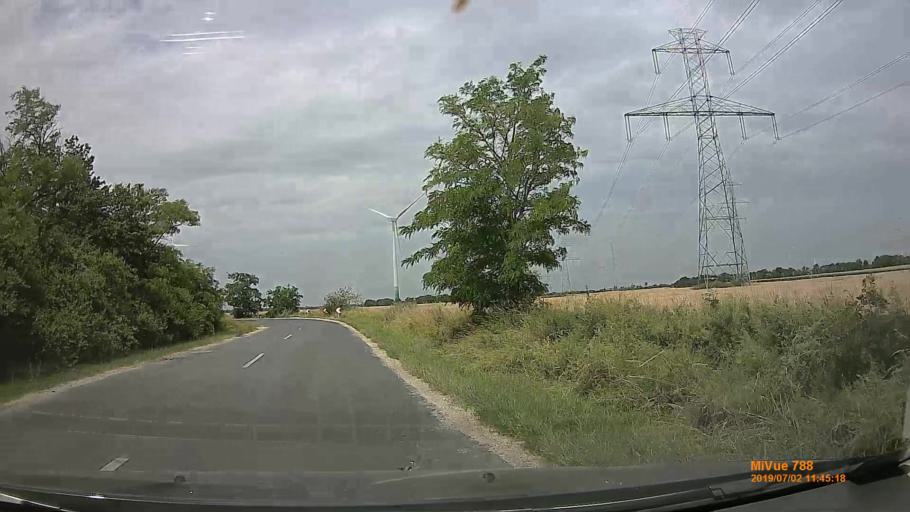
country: HU
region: Gyor-Moson-Sopron
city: Mosonmagyarovar
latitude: 47.8669
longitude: 17.1944
